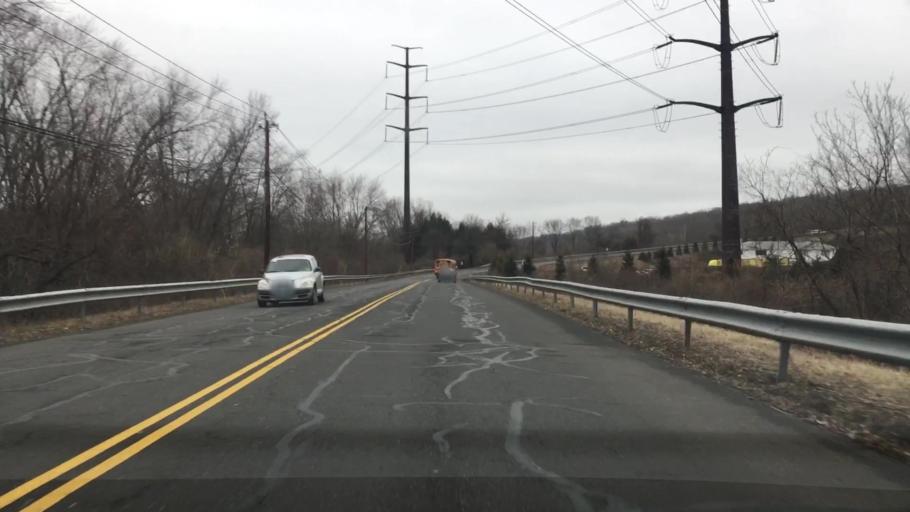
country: US
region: Connecticut
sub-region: Fairfield County
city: Bethel
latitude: 41.4417
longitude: -73.3965
